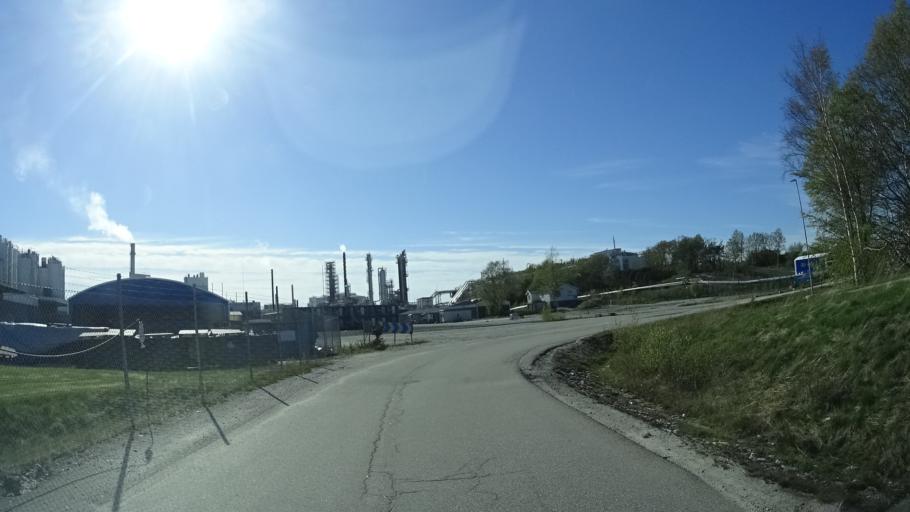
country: SE
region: Vaestra Goetaland
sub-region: Stenungsunds Kommun
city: Stenungsund
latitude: 58.0823
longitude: 11.8172
